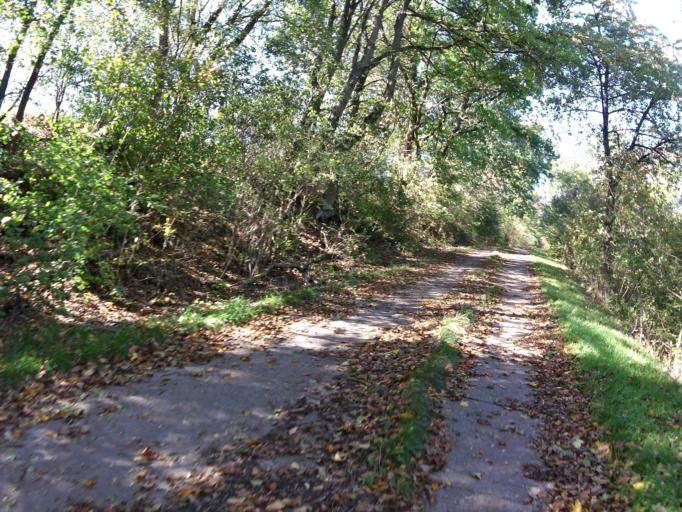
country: DE
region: Bavaria
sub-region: Regierungsbezirk Unterfranken
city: Hettstadt
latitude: 49.8289
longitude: 9.8293
